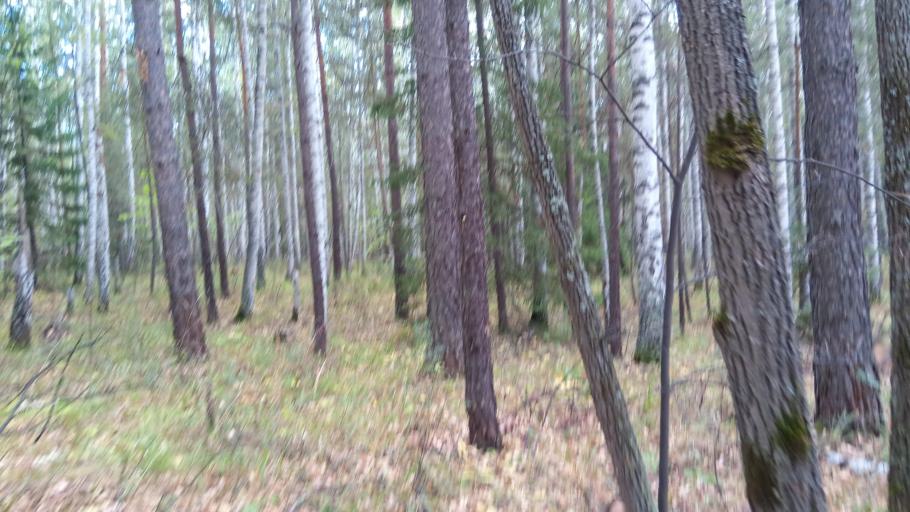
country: RU
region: Chelyabinsk
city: Turgoyak
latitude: 55.1814
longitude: 60.0245
